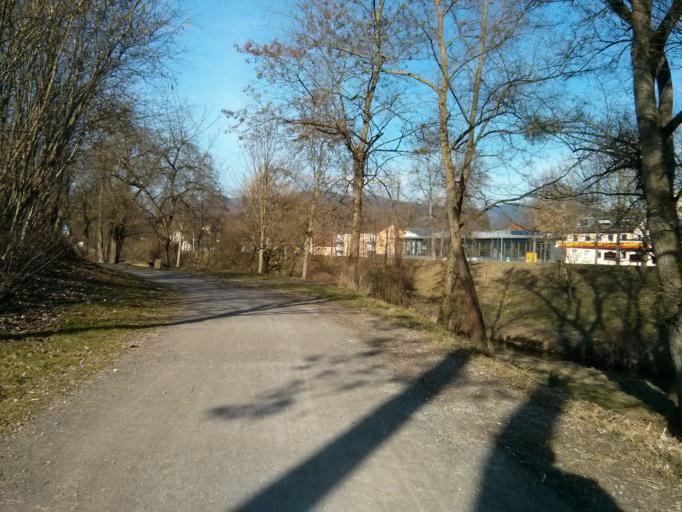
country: DE
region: Bavaria
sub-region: Lower Bavaria
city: Deggendorf
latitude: 48.8401
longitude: 12.9583
